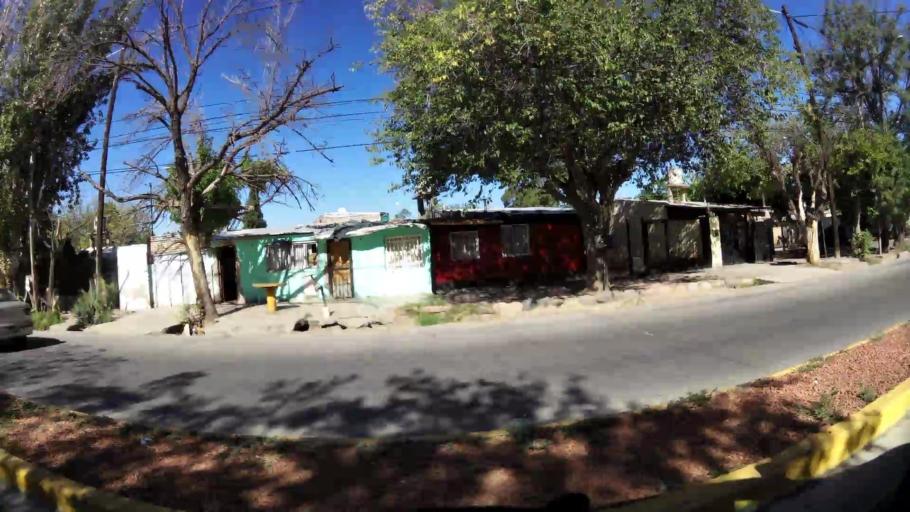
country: AR
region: Mendoza
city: Las Heras
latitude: -32.8402
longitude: -68.8187
